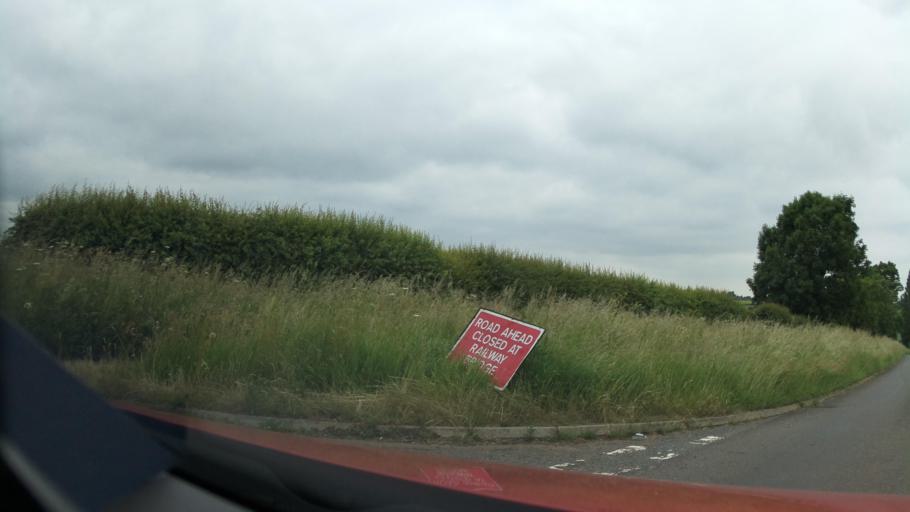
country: GB
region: England
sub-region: District of Rutland
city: Uppingham
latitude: 52.5996
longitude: -0.7229
